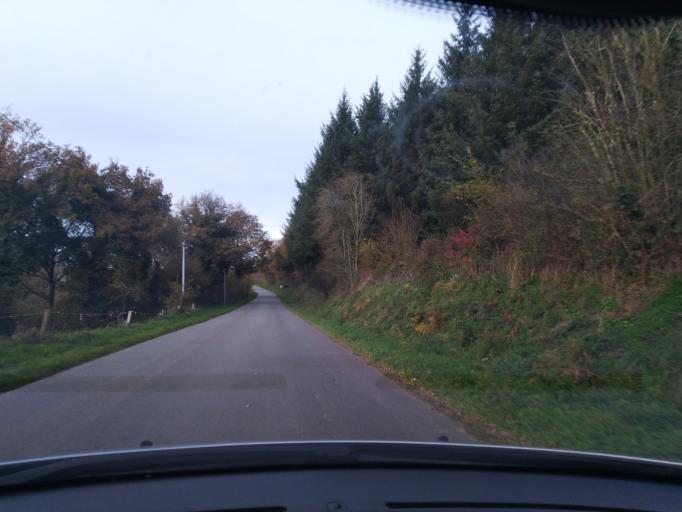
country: FR
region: Brittany
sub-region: Departement du Finistere
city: Guerlesquin
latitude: 48.5389
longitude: -3.6169
